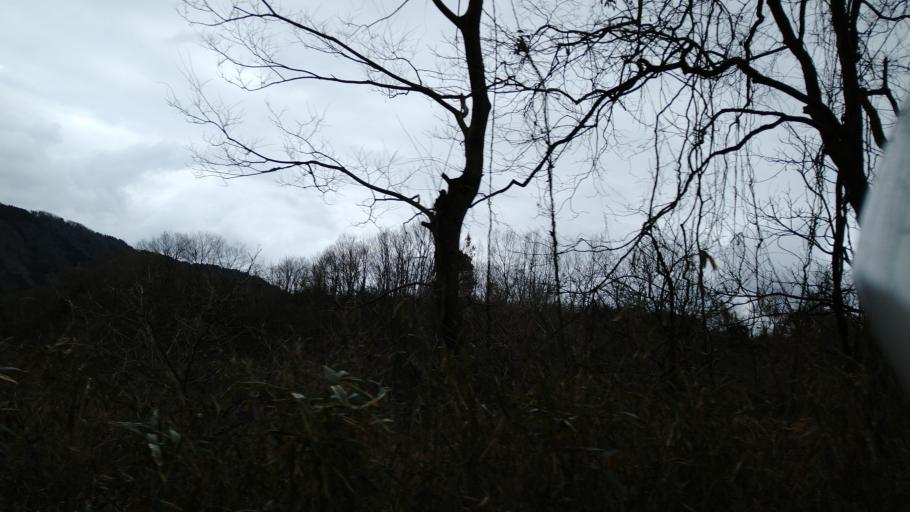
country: JP
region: Kyoto
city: Ayabe
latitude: 35.3200
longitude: 135.3608
